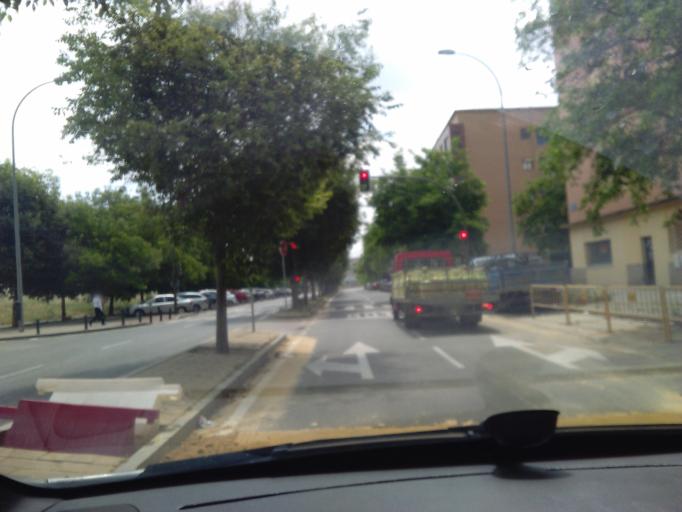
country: ES
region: Andalusia
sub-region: Provincia de Sevilla
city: Sevilla
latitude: 37.3668
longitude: -5.9523
